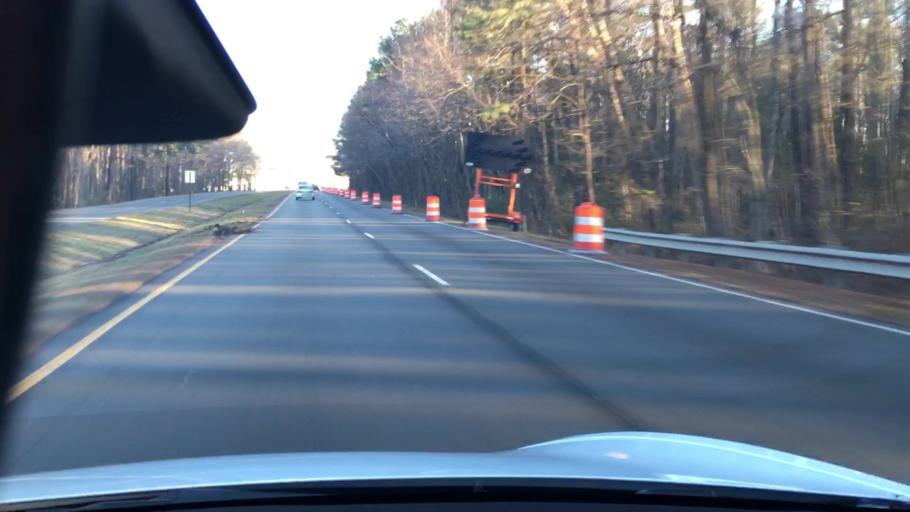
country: US
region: Virginia
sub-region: Henrico County
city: Fort Lee
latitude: 37.4898
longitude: -77.3539
